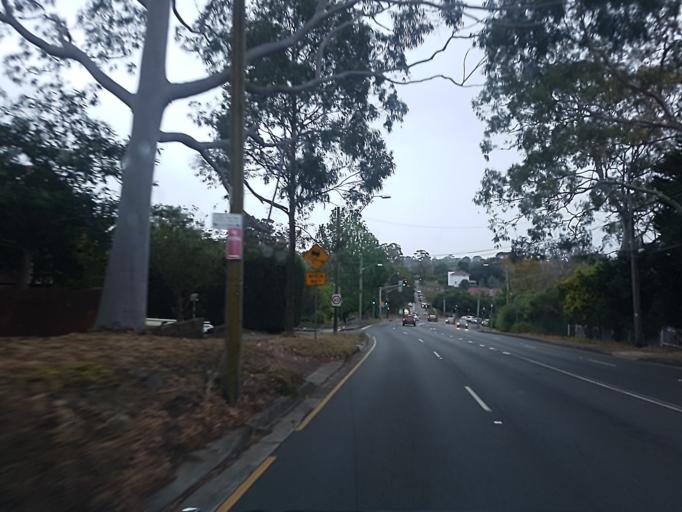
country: AU
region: New South Wales
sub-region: Willoughby
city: Castle Cove
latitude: -33.7928
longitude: 151.2074
